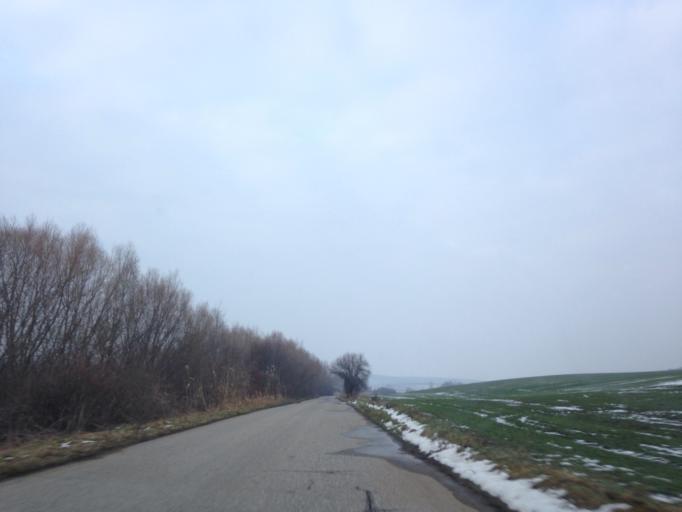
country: SK
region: Nitriansky
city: Svodin
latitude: 48.0446
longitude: 18.3704
